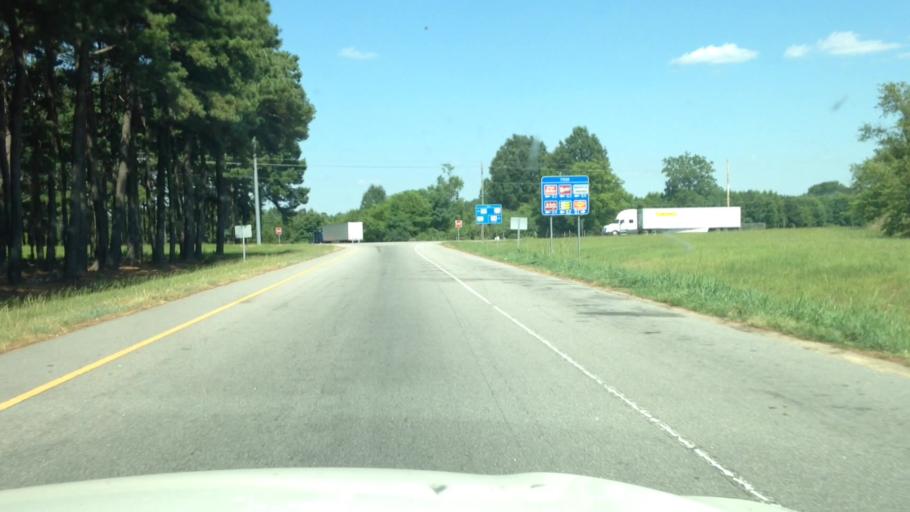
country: US
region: North Carolina
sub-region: Johnston County
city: Kenly
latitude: 35.5772
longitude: -78.1475
